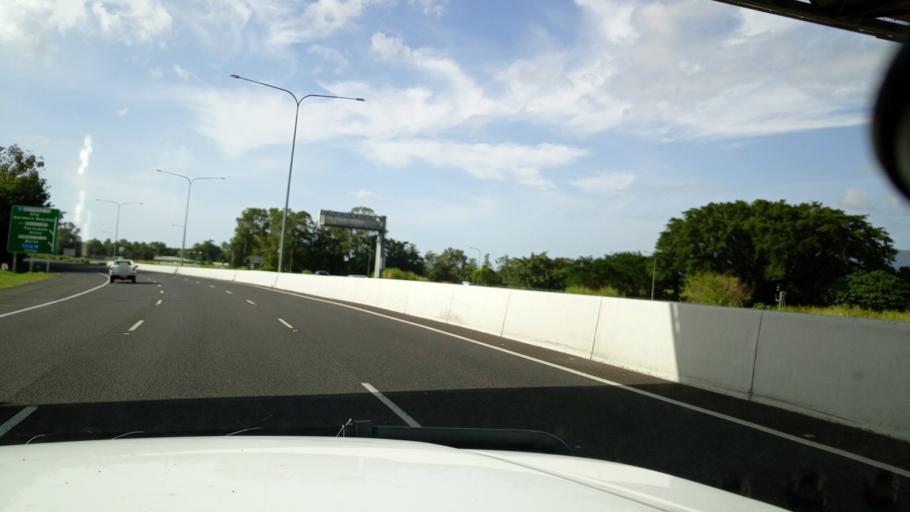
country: AU
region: Queensland
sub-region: Cairns
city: Woree
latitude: -16.9677
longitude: 145.7465
